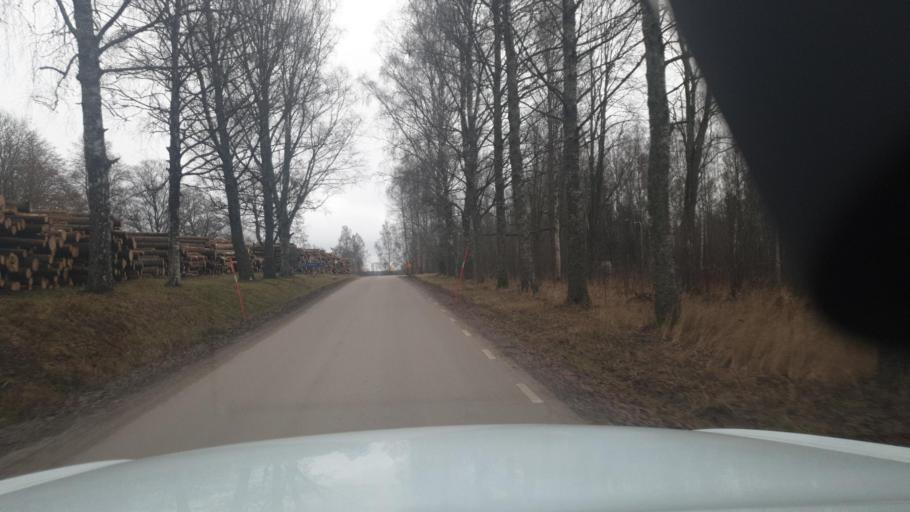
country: SE
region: Vaermland
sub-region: Sunne Kommun
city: Sunne
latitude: 59.7959
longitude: 13.1263
